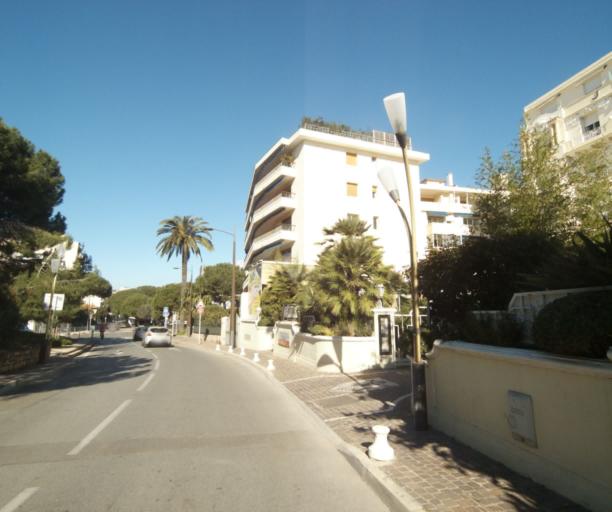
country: FR
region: Provence-Alpes-Cote d'Azur
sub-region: Departement des Alpes-Maritimes
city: Antibes
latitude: 43.5674
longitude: 7.1159
